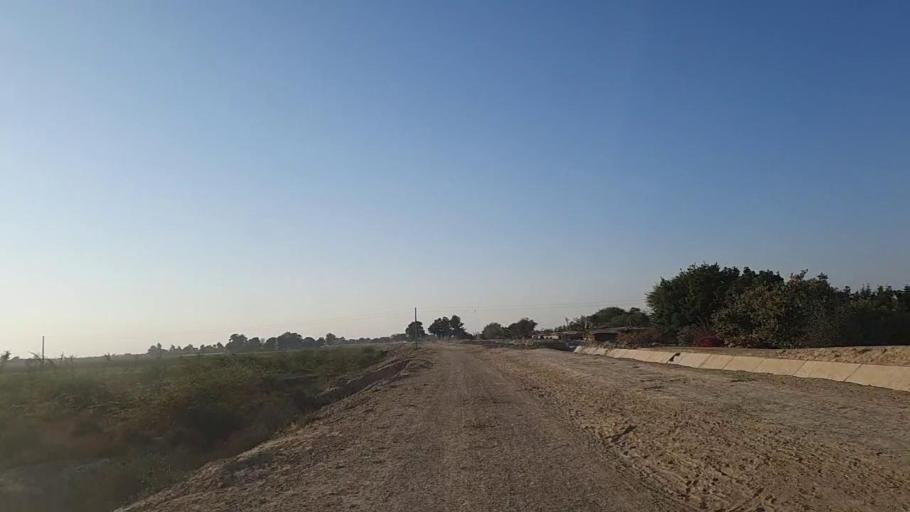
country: PK
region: Sindh
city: Naukot
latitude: 25.0039
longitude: 69.3937
